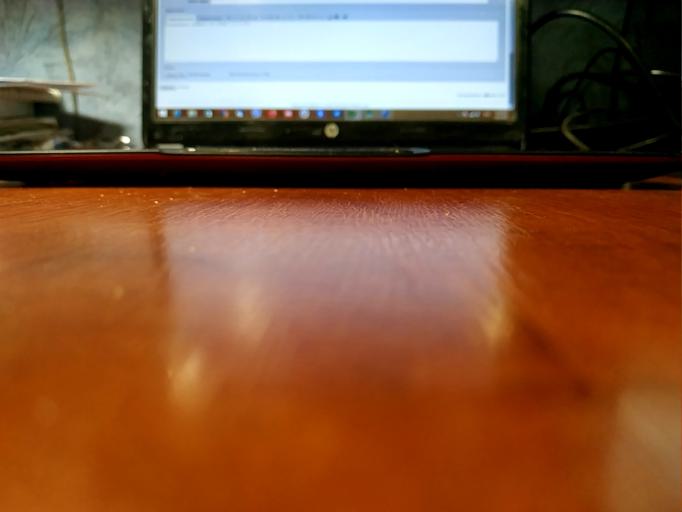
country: RU
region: Tverskaya
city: Sandovo
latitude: 58.4825
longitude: 36.3743
